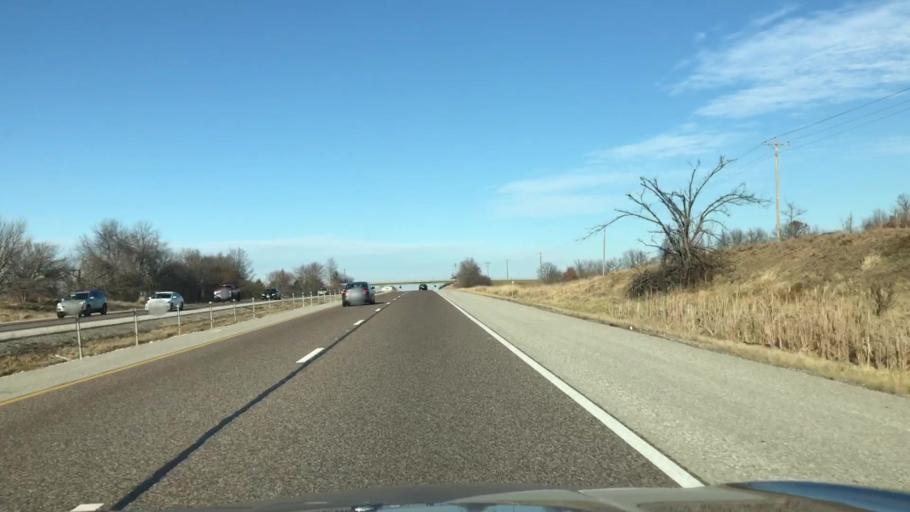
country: US
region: Illinois
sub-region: Madison County
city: Troy
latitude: 38.7788
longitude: -89.8997
